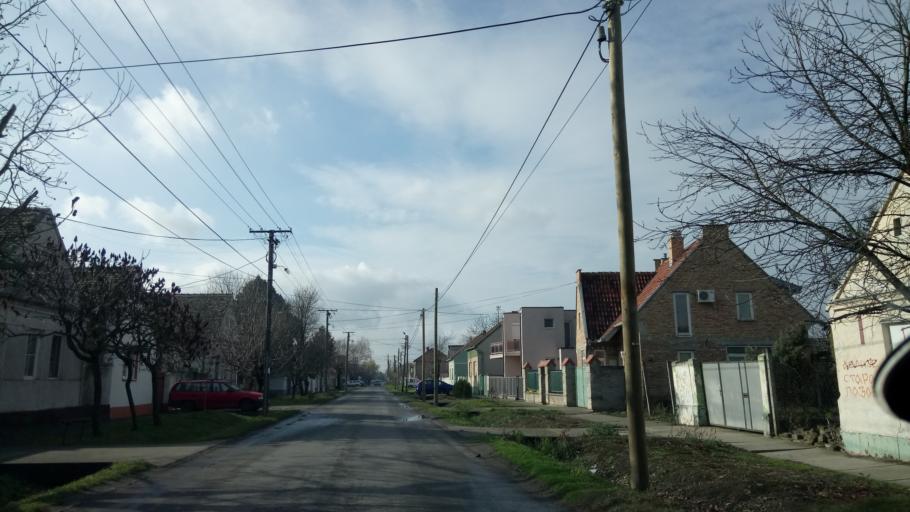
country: RS
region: Autonomna Pokrajina Vojvodina
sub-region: Sremski Okrug
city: Stara Pazova
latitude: 44.9816
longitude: 20.1524
